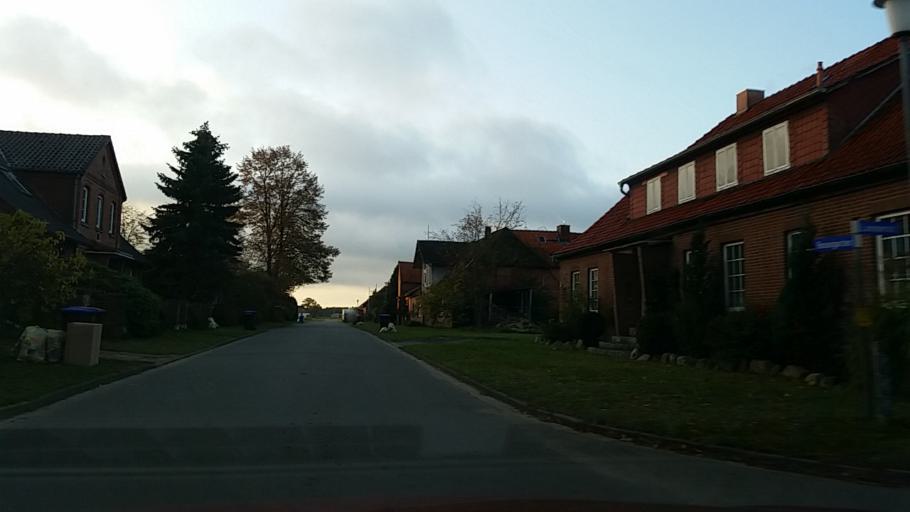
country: DE
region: Lower Saxony
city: Luder
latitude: 52.8105
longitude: 10.6709
